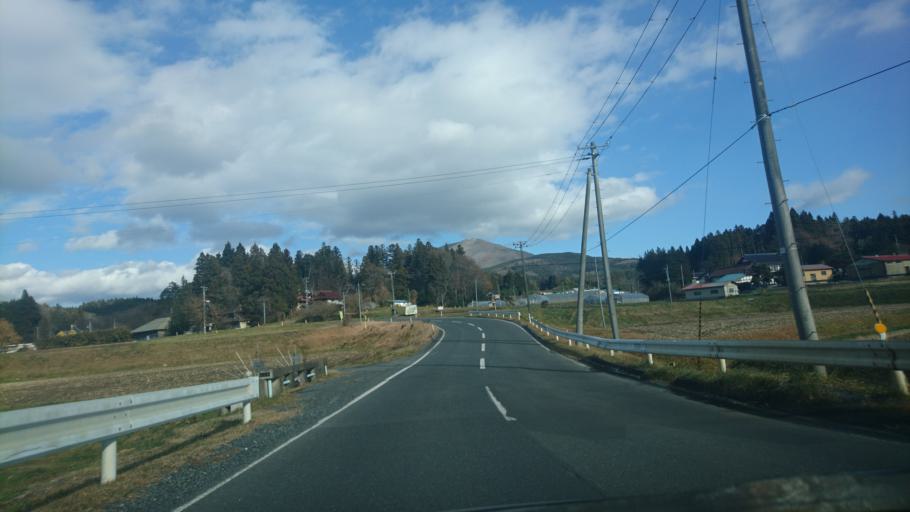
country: JP
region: Iwate
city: Ichinoseki
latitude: 38.9463
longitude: 141.4065
